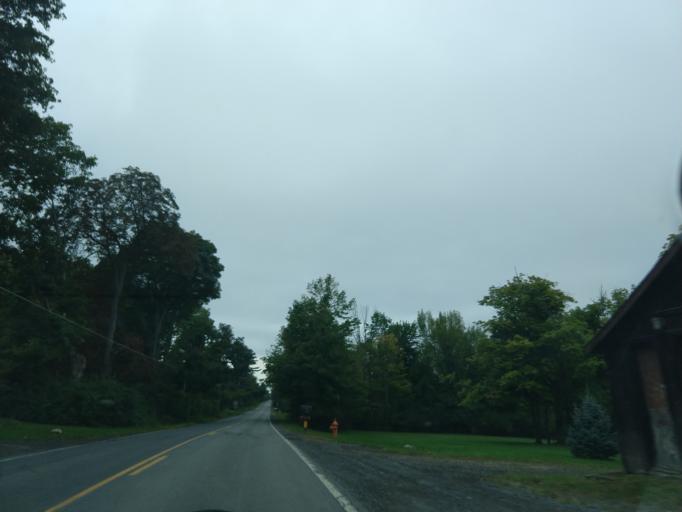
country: US
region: New York
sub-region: Tompkins County
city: East Ithaca
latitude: 42.4079
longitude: -76.4693
